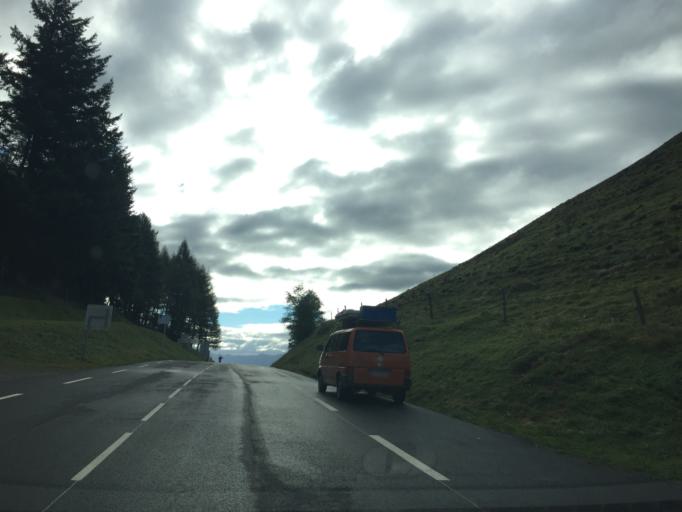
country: FR
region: Midi-Pyrenees
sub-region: Departement de la Haute-Garonne
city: Bagneres-de-Luchon
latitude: 42.8022
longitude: 0.4617
